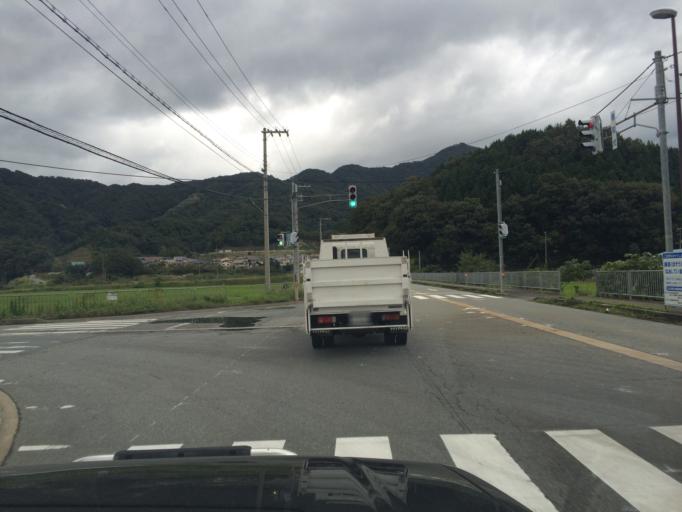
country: JP
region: Hyogo
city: Toyooka
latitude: 35.4338
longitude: 134.7963
